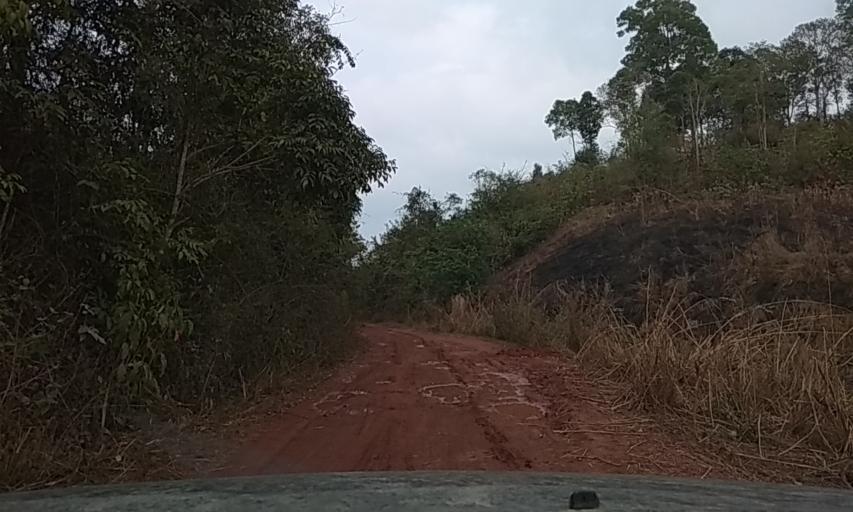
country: TH
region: Nan
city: Mae Charim
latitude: 18.4350
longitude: 101.1824
